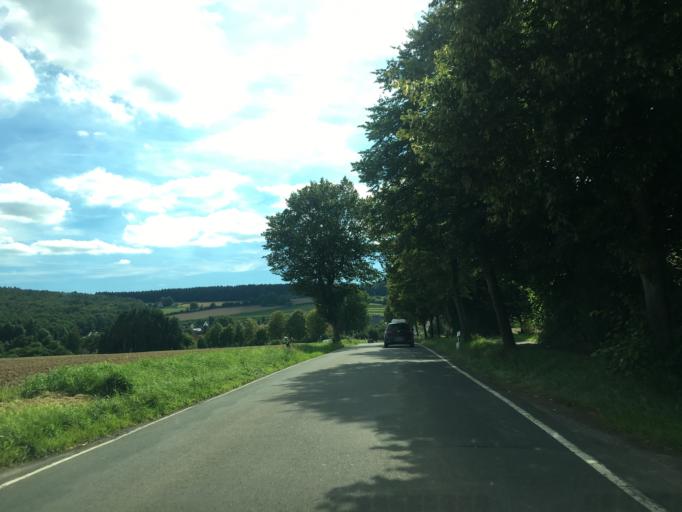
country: DE
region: North Rhine-Westphalia
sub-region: Regierungsbezirk Detmold
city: Barntrup
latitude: 51.9851
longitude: 9.0866
